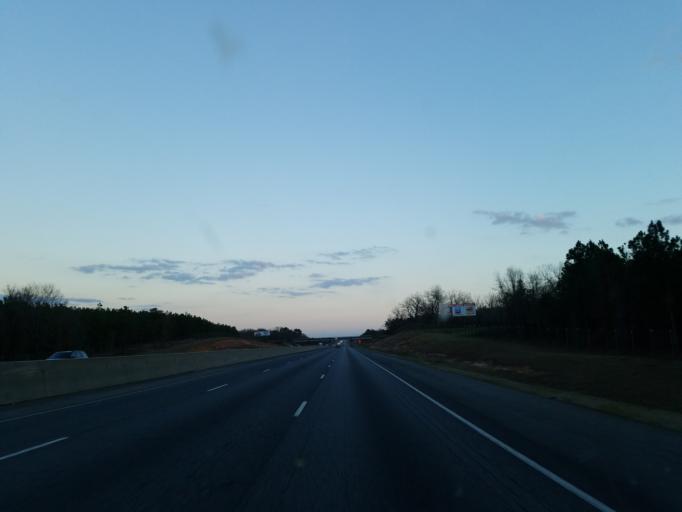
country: US
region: Georgia
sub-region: Turner County
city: Ashburn
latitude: 31.7916
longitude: -83.6945
